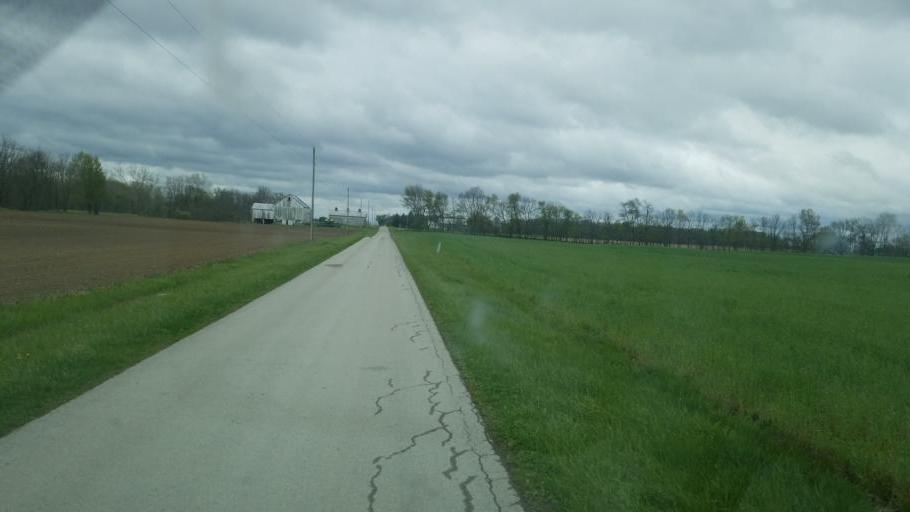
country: US
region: Ohio
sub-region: Wyandot County
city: Upper Sandusky
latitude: 40.7554
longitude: -83.1450
